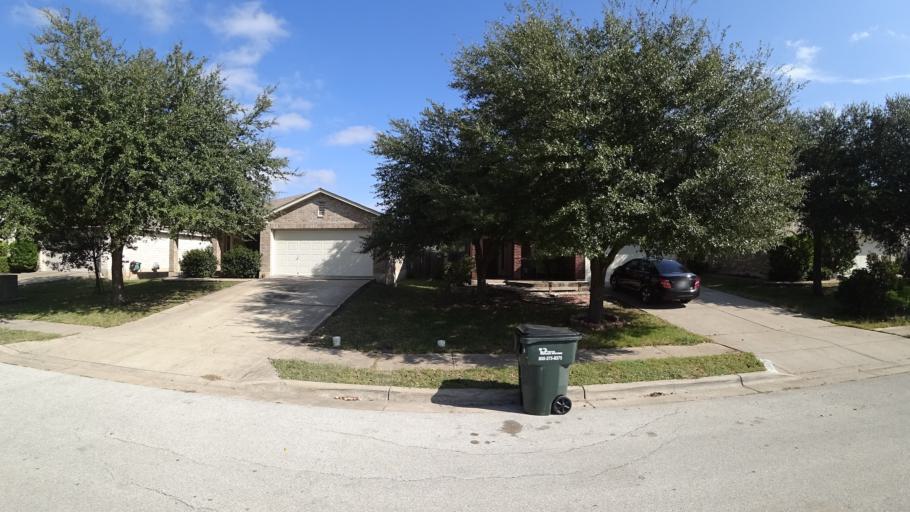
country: US
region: Texas
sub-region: Travis County
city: Pflugerville
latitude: 30.4171
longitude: -97.6390
